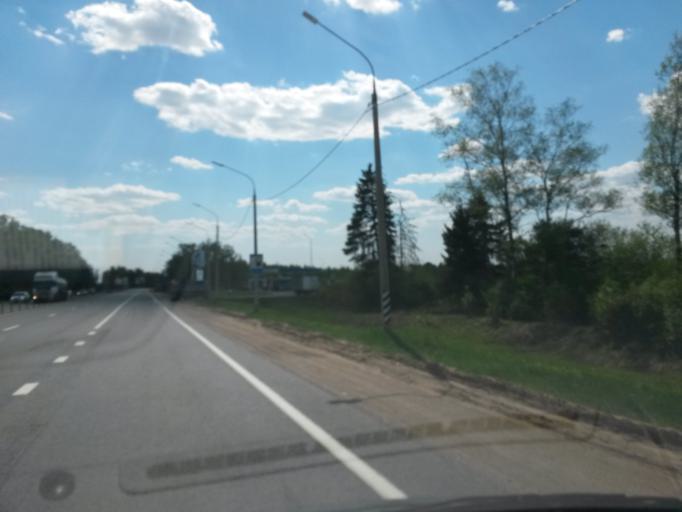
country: RU
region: Jaroslavl
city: Semibratovo
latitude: 57.3427
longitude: 39.5815
